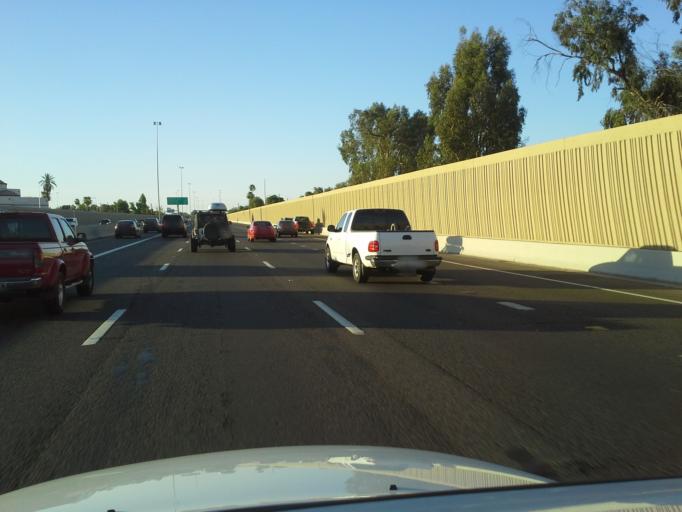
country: US
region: Arizona
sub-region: Maricopa County
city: Glendale
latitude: 33.5437
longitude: -112.1122
